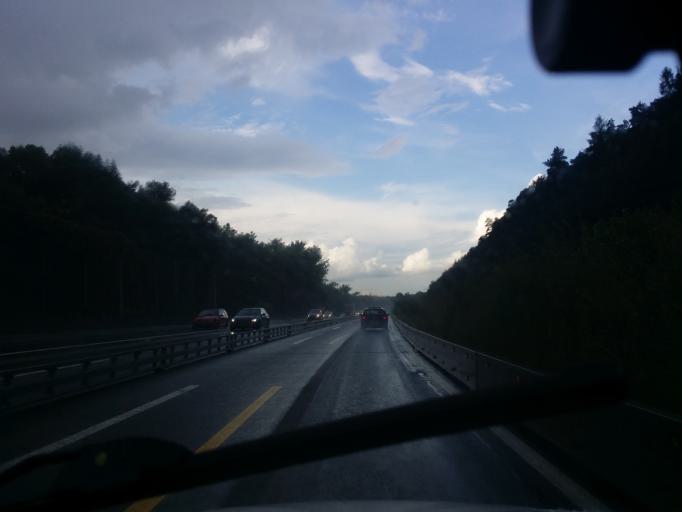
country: DE
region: Hesse
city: Schwarzenborn
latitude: 50.9764
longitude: 9.4732
